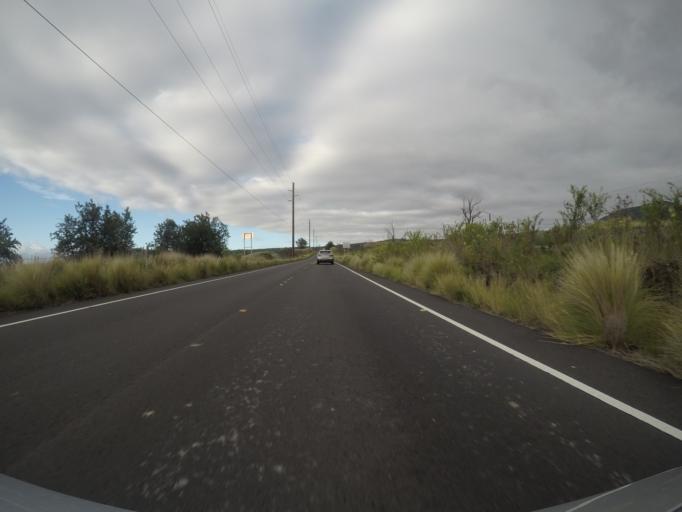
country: US
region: Hawaii
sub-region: Hawaii County
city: Kalaoa
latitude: 19.7958
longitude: -155.8649
